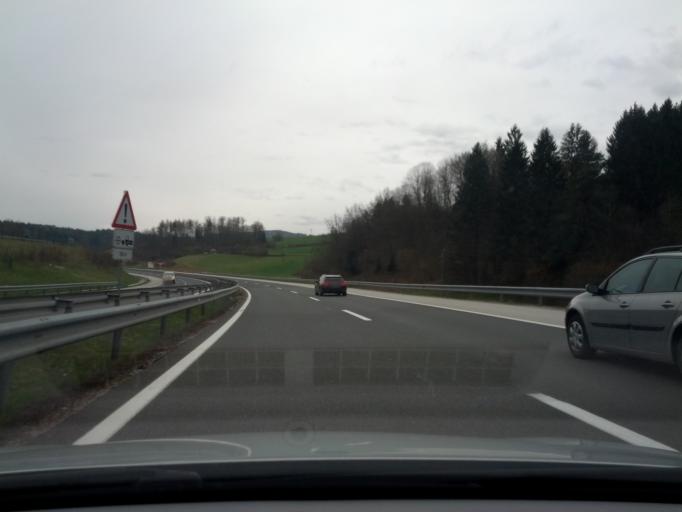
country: SI
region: Trebnje
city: Trebnje
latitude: 45.9221
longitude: 14.9408
